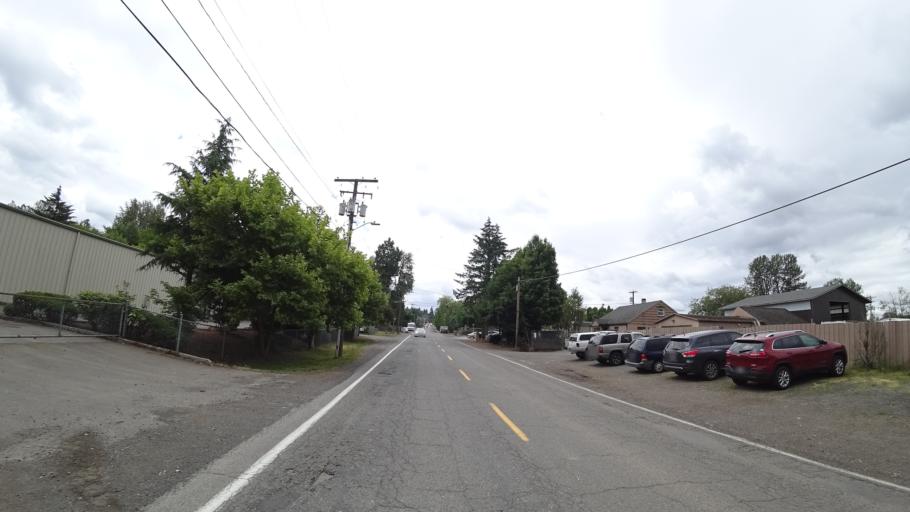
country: US
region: Washington
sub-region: Clark County
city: Vancouver
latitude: 45.5758
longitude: -122.6140
